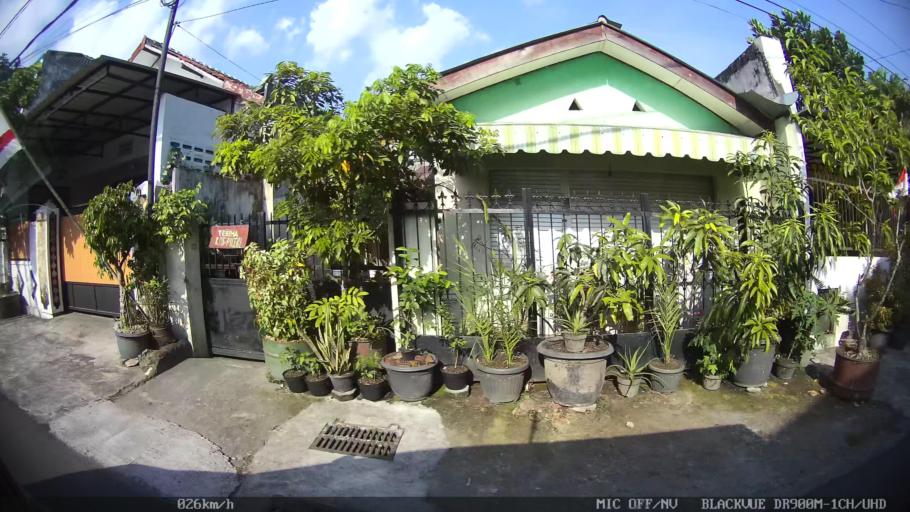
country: ID
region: Daerah Istimewa Yogyakarta
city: Yogyakarta
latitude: -7.8175
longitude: 110.3816
